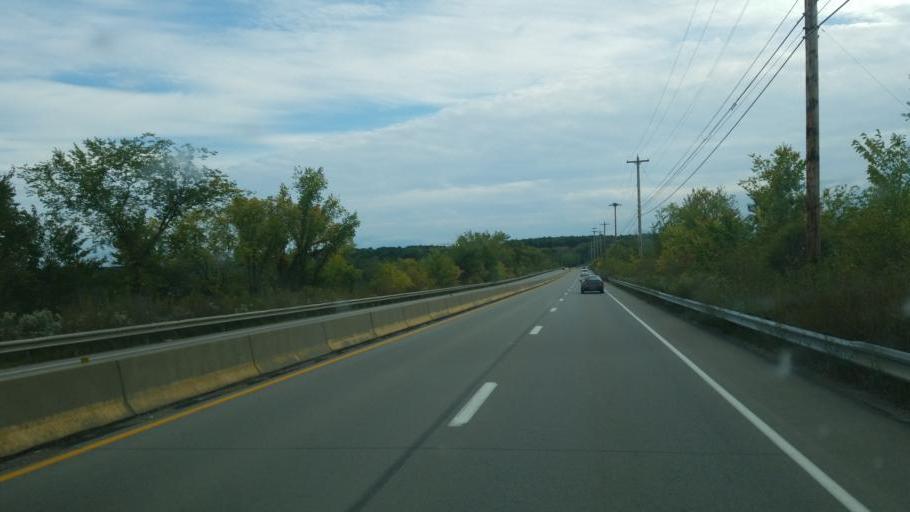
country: US
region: Pennsylvania
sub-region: Mercer County
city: Sharpsville
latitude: 41.2907
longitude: -80.4274
